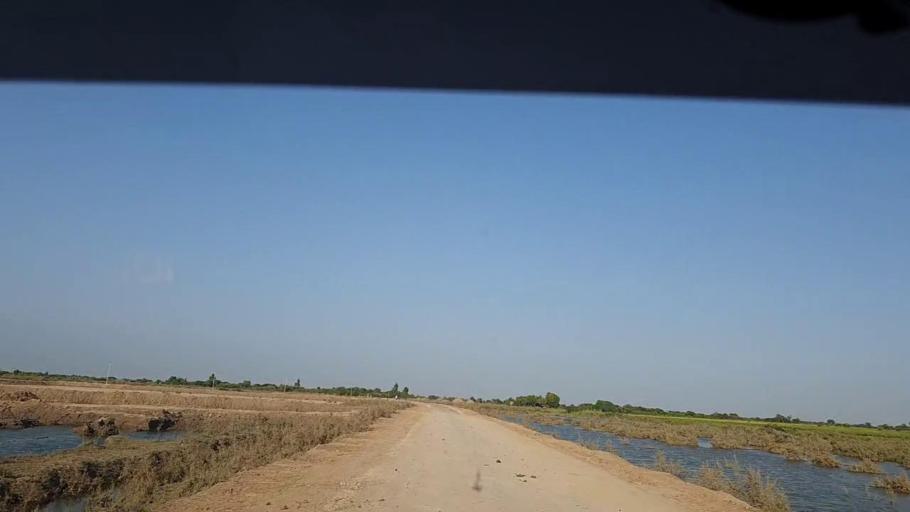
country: PK
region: Sindh
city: Badin
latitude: 24.6947
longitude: 68.8566
